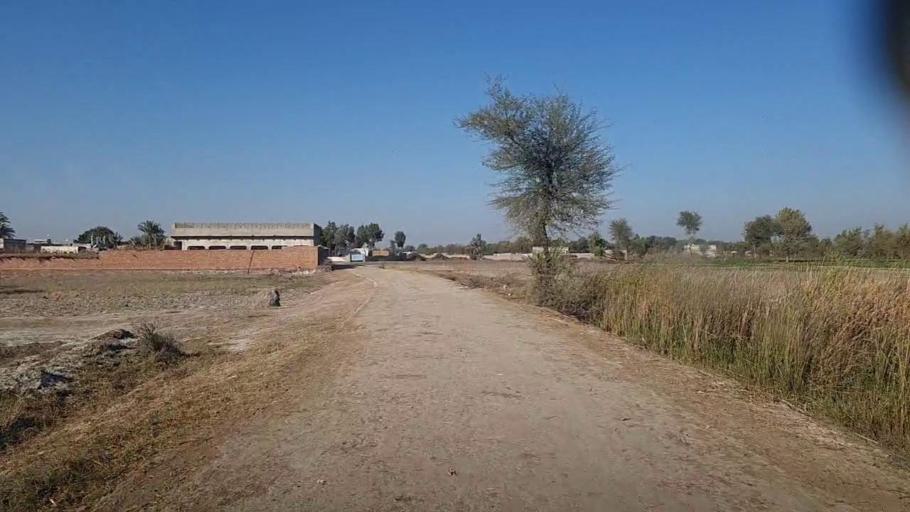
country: PK
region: Sindh
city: Khairpur
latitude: 28.0002
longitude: 69.7330
